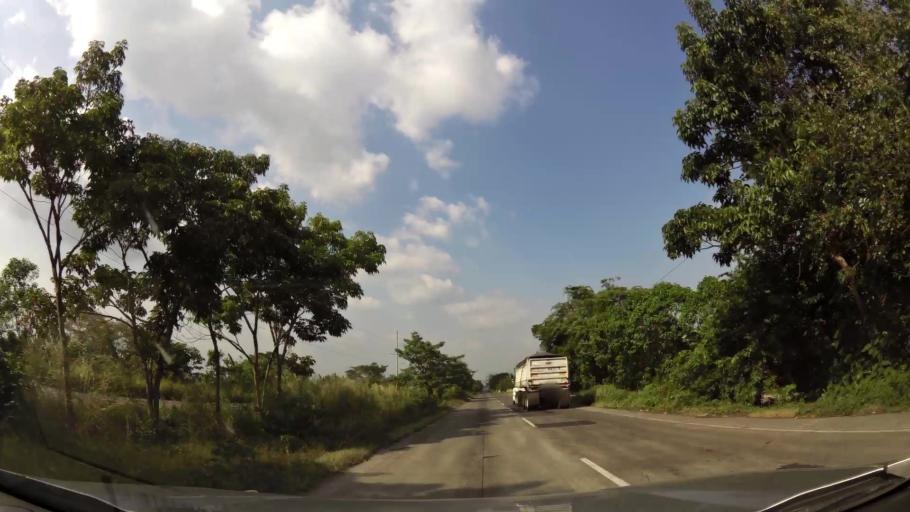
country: GT
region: Escuintla
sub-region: Municipio de Masagua
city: Masagua
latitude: 14.0855
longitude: -90.7785
